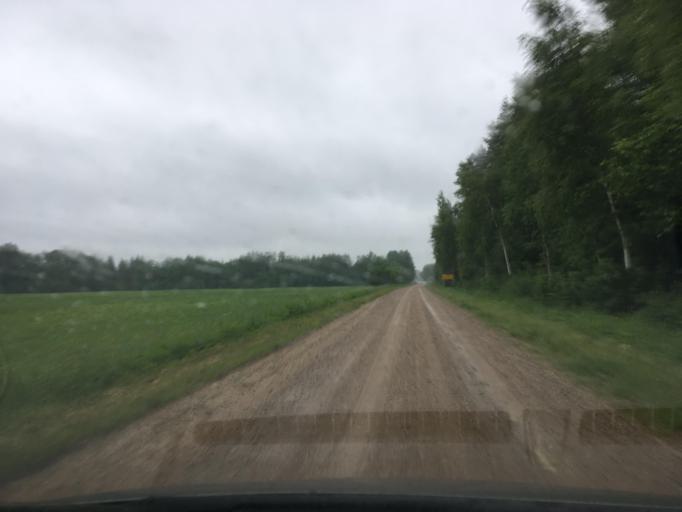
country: EE
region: Laeaene
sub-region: Lihula vald
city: Lihula
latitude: 58.6238
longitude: 23.8197
